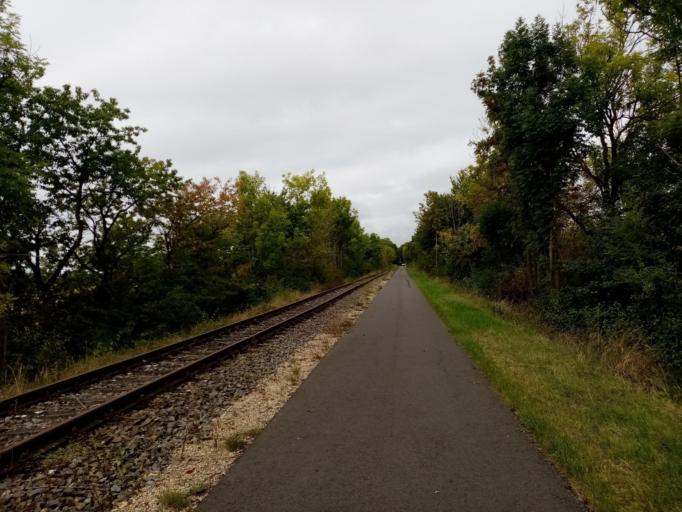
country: DE
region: Thuringia
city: Dingelstadt
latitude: 51.3011
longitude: 10.3073
